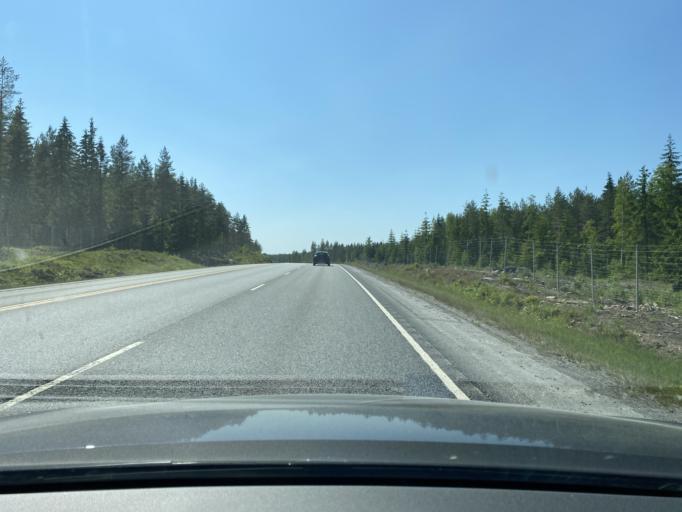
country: FI
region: Pirkanmaa
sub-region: Lounais-Pirkanmaa
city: Mouhijaervi
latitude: 61.3953
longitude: 23.2357
